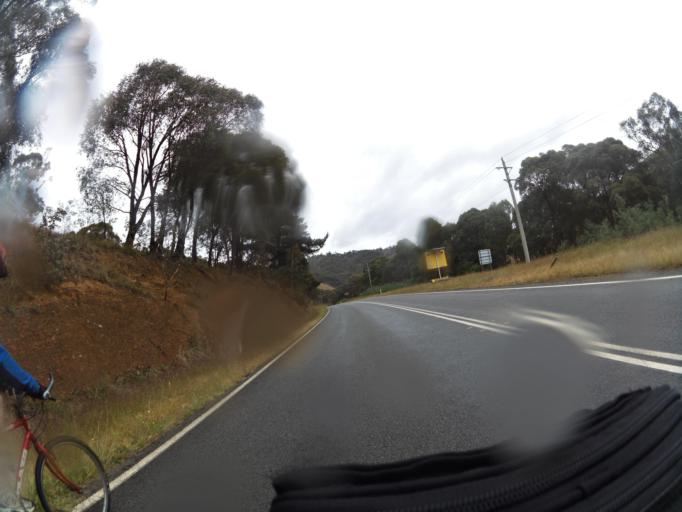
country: AU
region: New South Wales
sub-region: Greater Hume Shire
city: Holbrook
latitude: -36.2187
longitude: 147.6735
